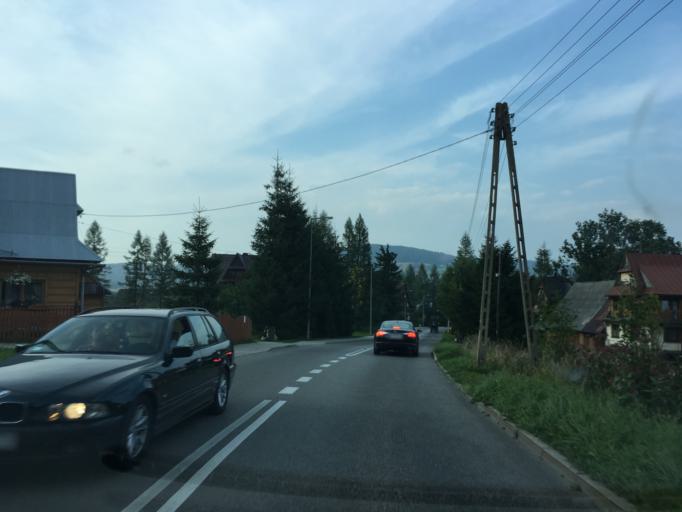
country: PL
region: Lesser Poland Voivodeship
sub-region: Powiat tatrzanski
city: Koscielisko
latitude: 49.2777
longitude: 19.8857
